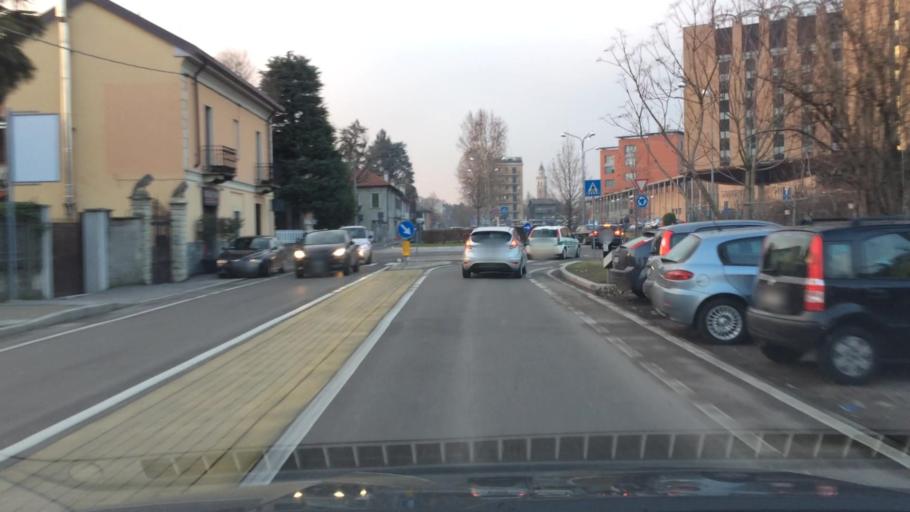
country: IT
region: Lombardy
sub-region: Provincia di Varese
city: Saronno
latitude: 45.6215
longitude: 9.0284
